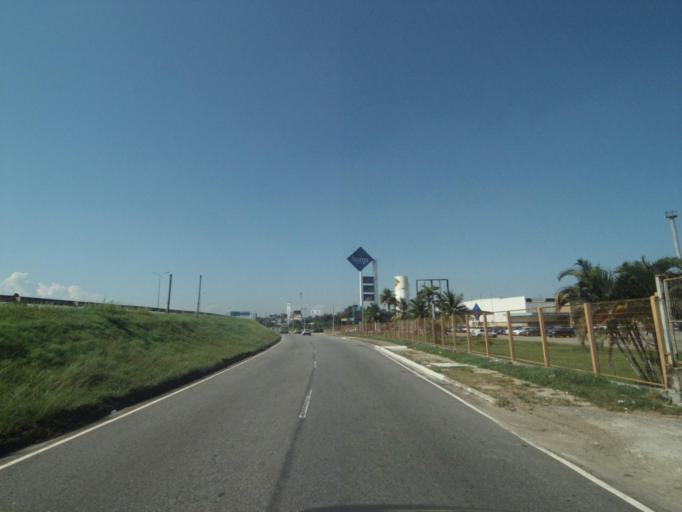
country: BR
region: Rio de Janeiro
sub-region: Niteroi
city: Niteroi
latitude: -22.8582
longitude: -43.1044
